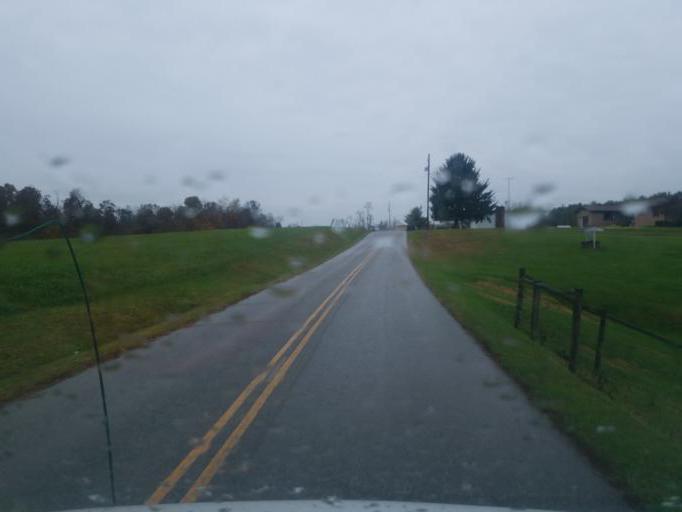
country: US
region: Ohio
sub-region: Washington County
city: Beverly
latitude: 39.4421
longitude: -81.6215
